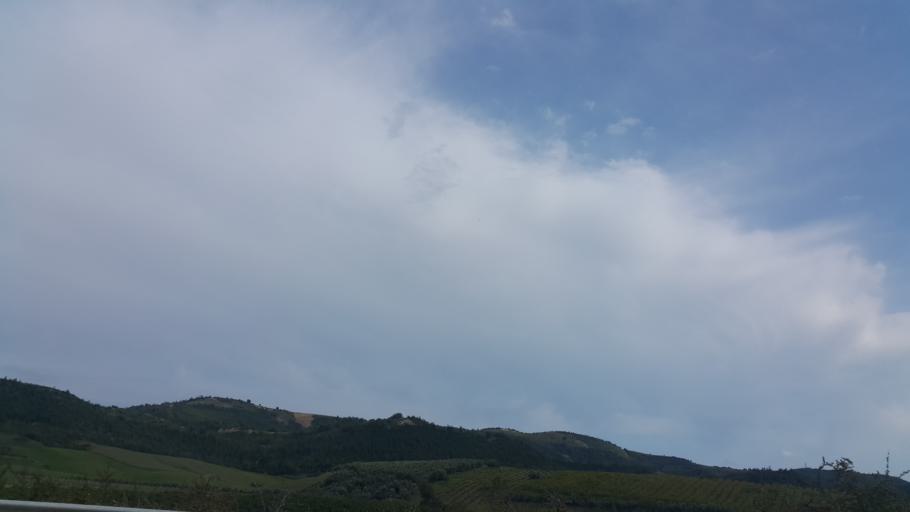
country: TR
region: Mersin
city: Kazanli
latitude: 36.9506
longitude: 34.7362
